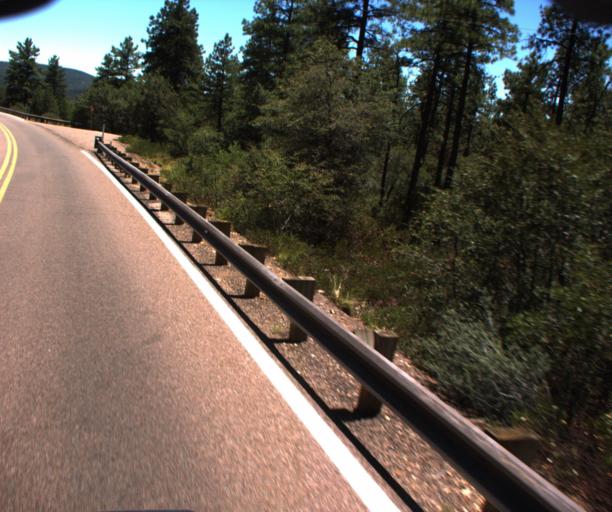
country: US
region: Arizona
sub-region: Gila County
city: Pine
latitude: 34.3953
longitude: -111.4679
